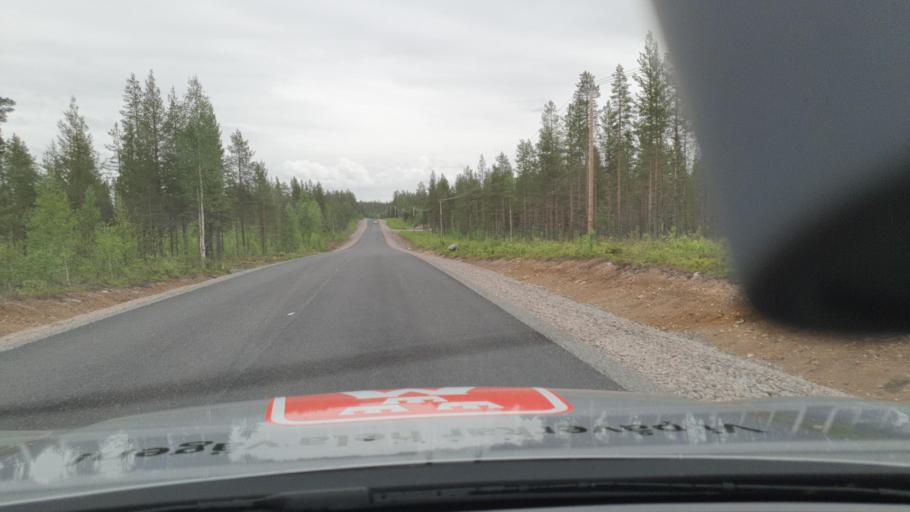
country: SE
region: Norrbotten
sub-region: Overtornea Kommun
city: OEvertornea
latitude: 66.6498
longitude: 23.2362
